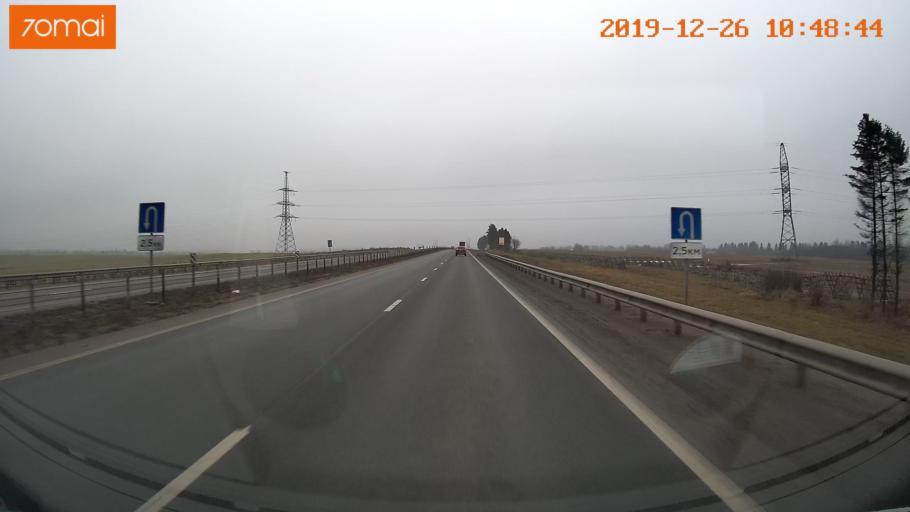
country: RU
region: Vologda
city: Molochnoye
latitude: 59.2120
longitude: 39.7342
